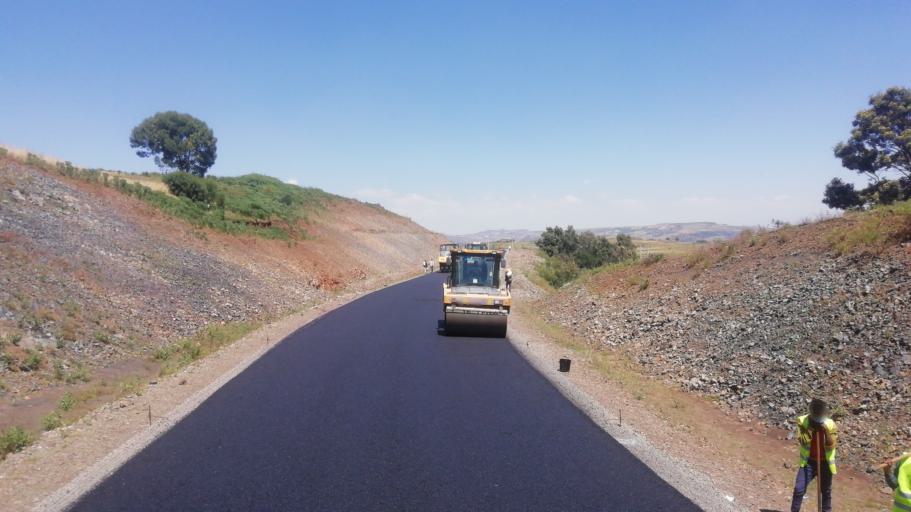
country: ET
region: Amhara
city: Addiet Canna
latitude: 11.3660
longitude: 37.8709
